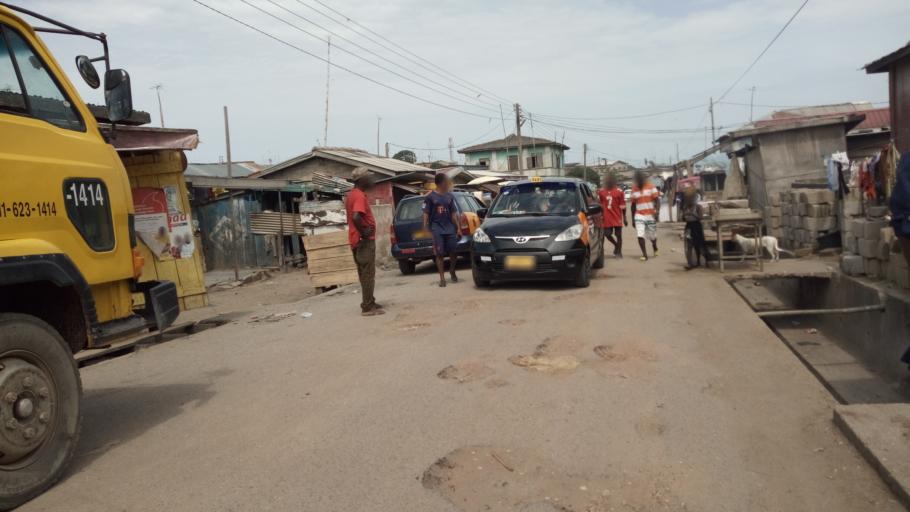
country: GH
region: Central
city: Winneba
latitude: 5.3452
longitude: -0.6198
